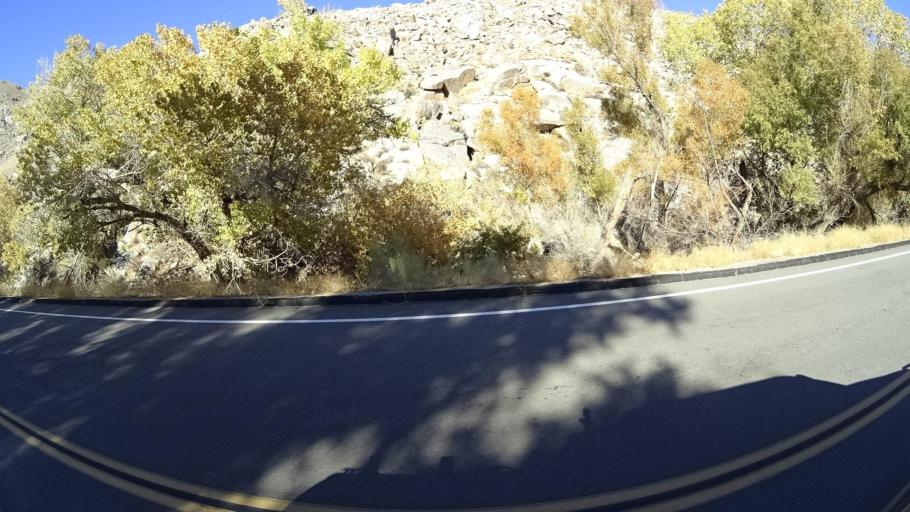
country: US
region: California
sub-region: Kern County
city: Weldon
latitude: 35.6731
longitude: -118.3415
